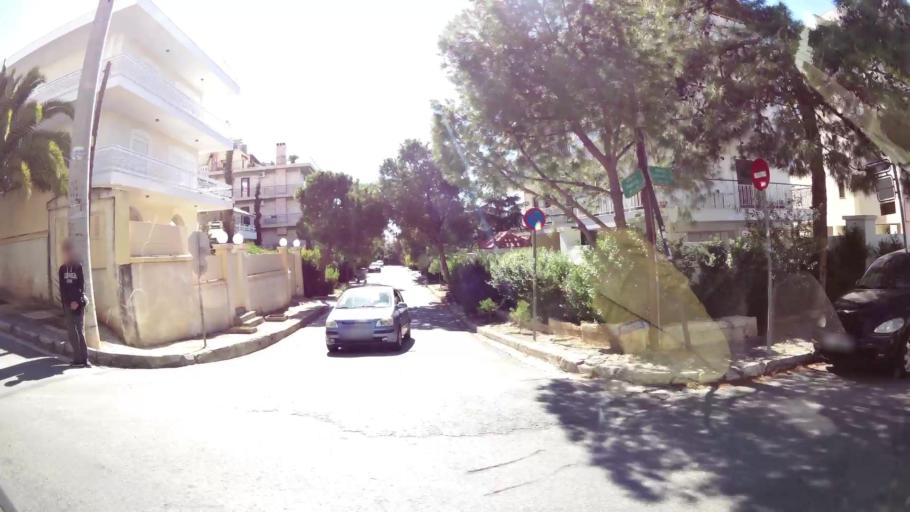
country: GR
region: Attica
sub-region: Nomarchia Anatolikis Attikis
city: Voula
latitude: 37.8468
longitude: 23.7745
